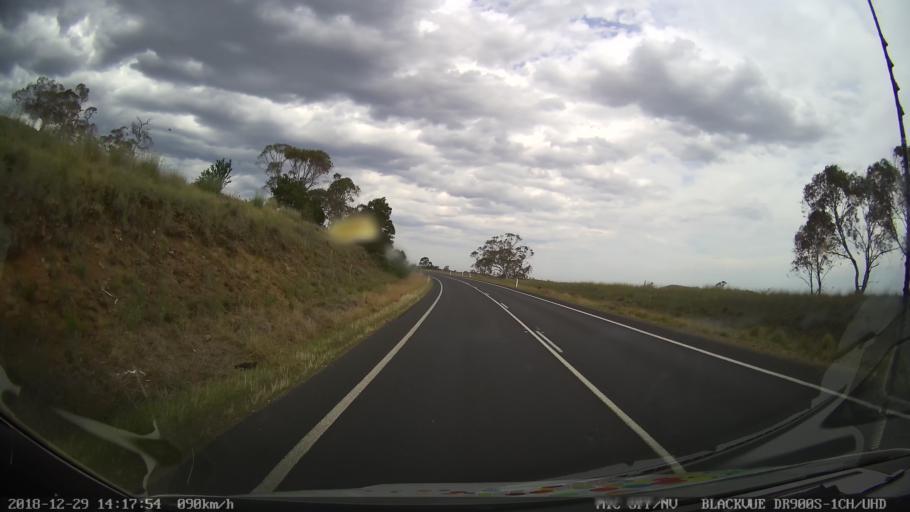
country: AU
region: New South Wales
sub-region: Cooma-Monaro
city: Cooma
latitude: -36.4847
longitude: 149.2617
